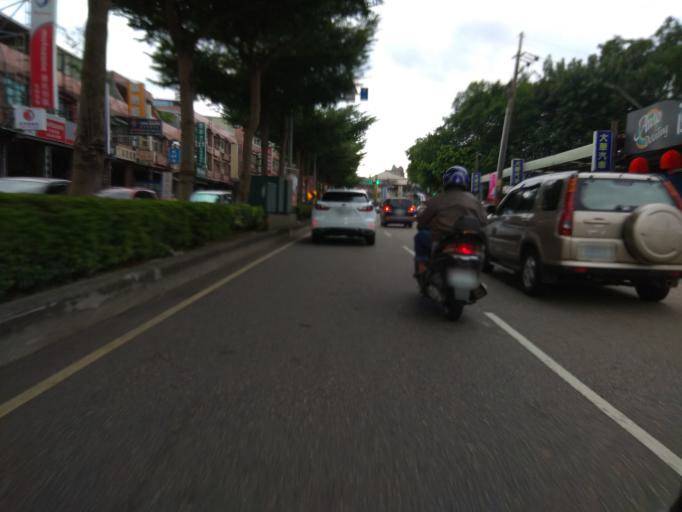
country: TW
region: Taiwan
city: Daxi
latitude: 24.9108
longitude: 121.2112
